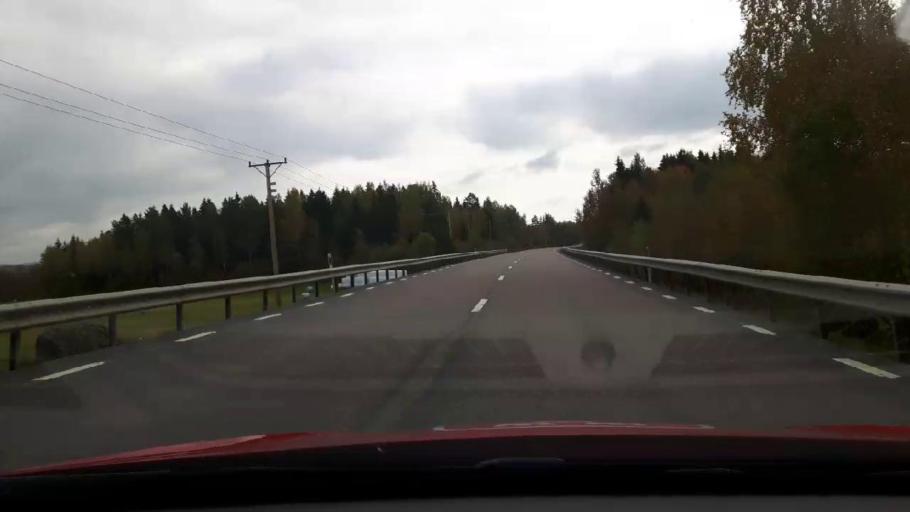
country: SE
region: Gaevleborg
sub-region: Bollnas Kommun
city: Kilafors
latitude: 61.2884
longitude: 16.5092
